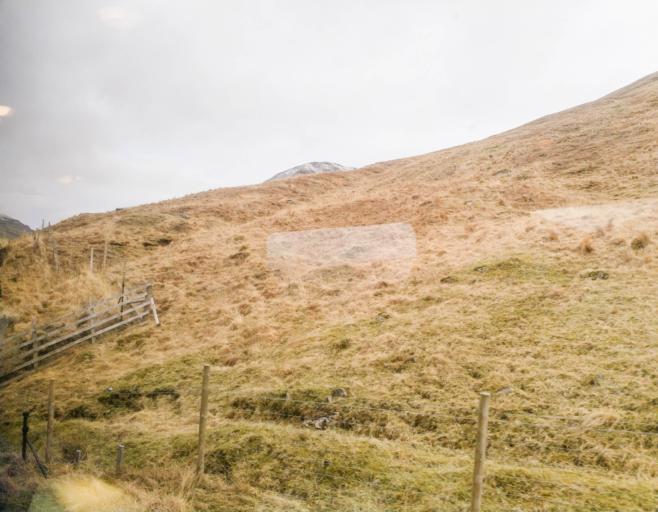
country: GB
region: Scotland
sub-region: Argyll and Bute
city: Garelochhead
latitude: 56.4753
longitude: -4.7175
